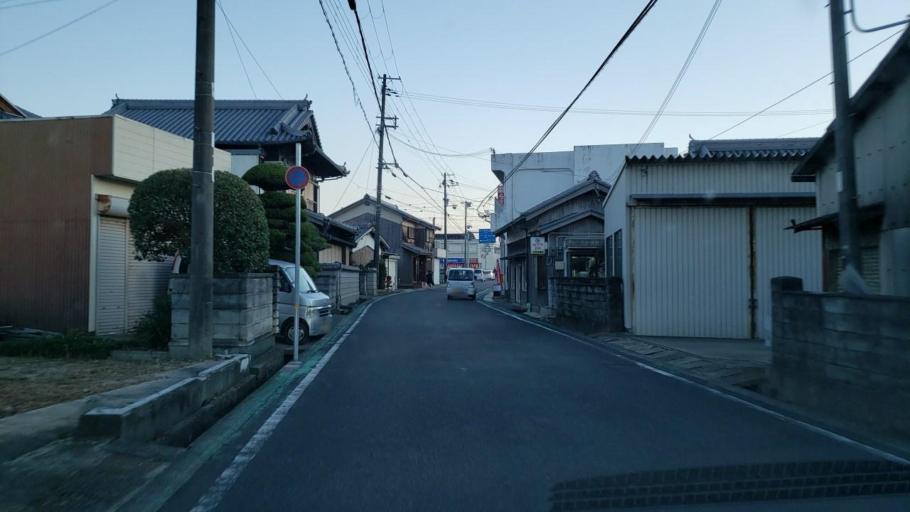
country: JP
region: Hyogo
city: Fukura
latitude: 34.3022
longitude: 134.7638
